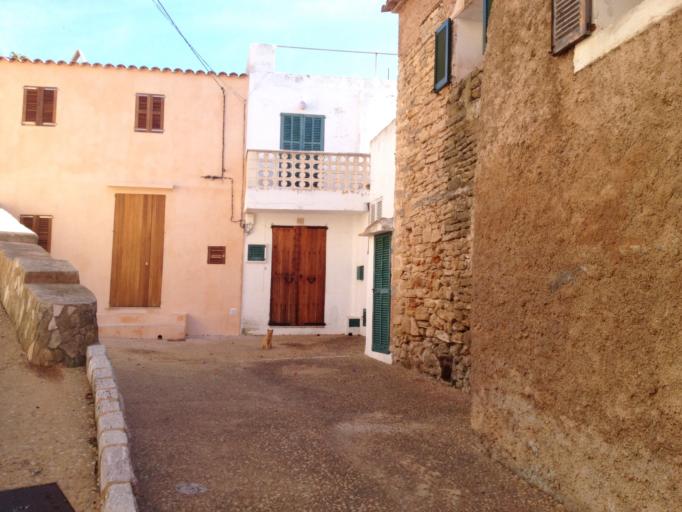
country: ES
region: Balearic Islands
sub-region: Illes Balears
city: Capdepera
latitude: 39.7039
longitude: 3.4324
